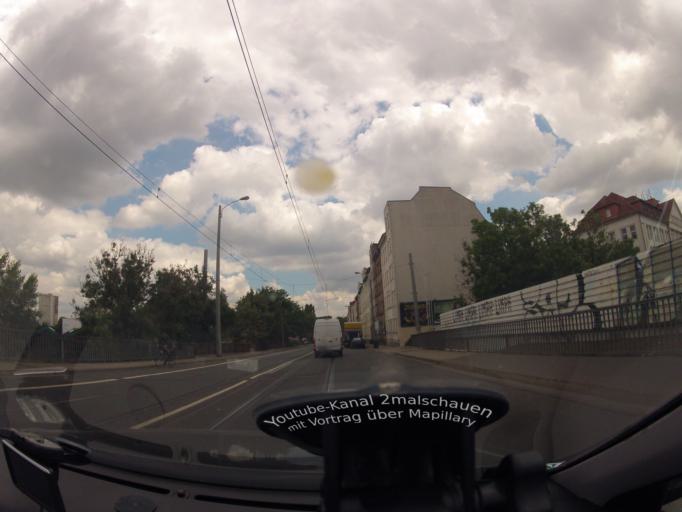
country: DE
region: Saxony
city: Leipzig
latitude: 51.3471
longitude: 12.4179
